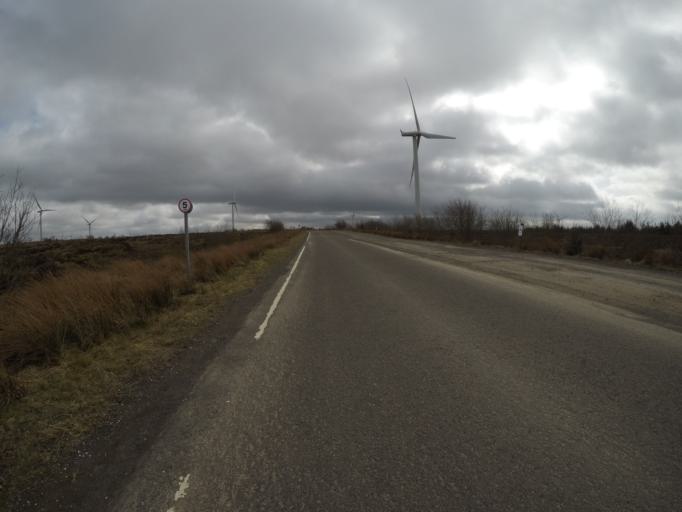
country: GB
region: Scotland
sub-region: East Renfrewshire
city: Newton Mearns
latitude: 55.7045
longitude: -4.3569
